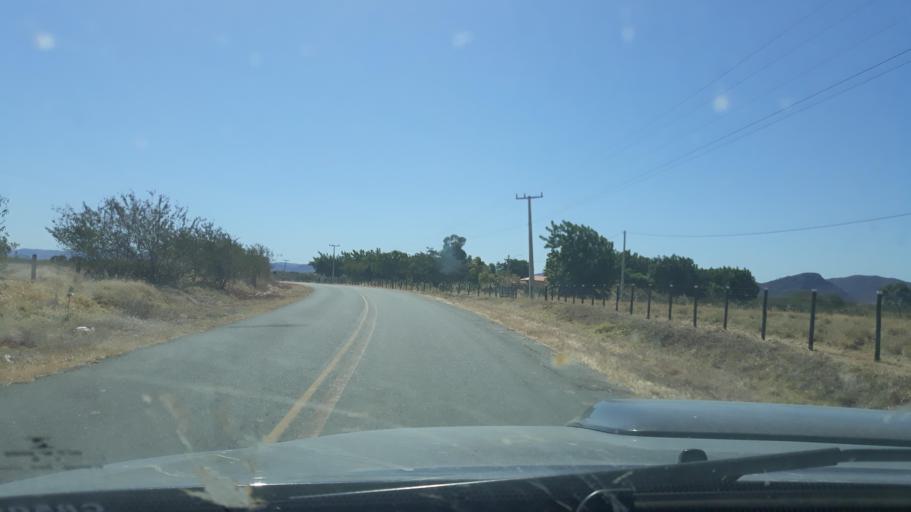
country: BR
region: Bahia
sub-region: Guanambi
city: Guanambi
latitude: -13.9607
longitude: -42.8557
